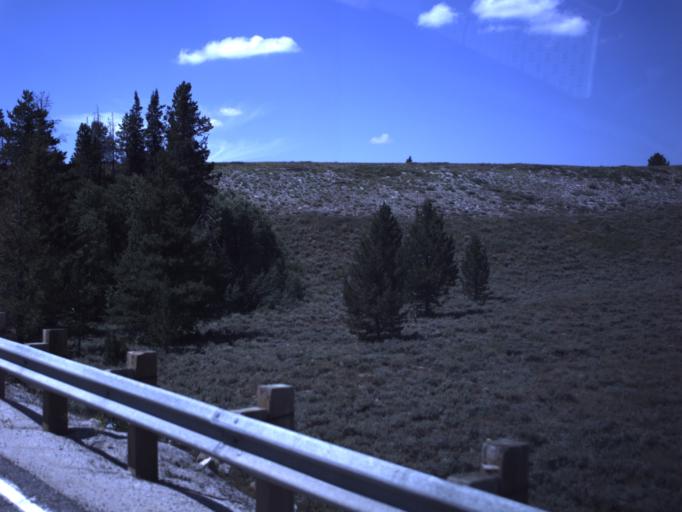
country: US
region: Idaho
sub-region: Bear Lake County
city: Paris
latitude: 41.9518
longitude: -111.4927
